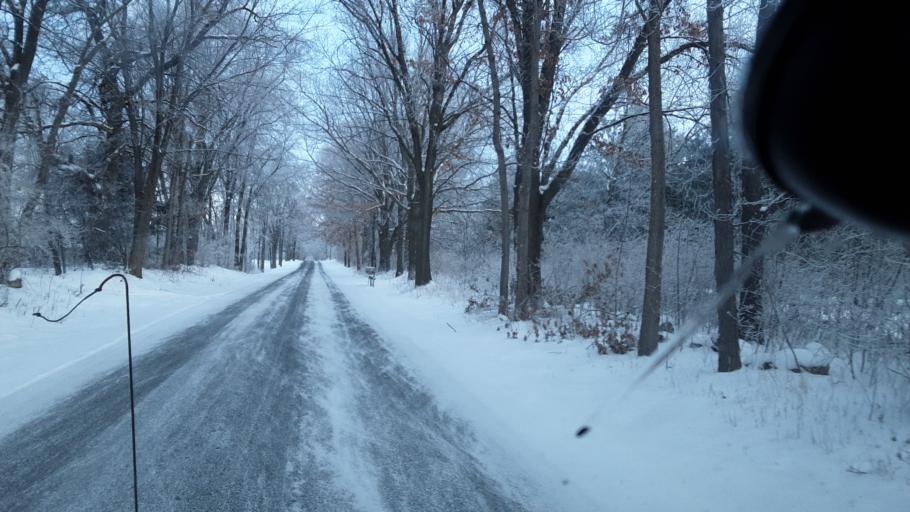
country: US
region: Michigan
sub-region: Ingham County
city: Leslie
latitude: 42.4258
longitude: -84.4970
